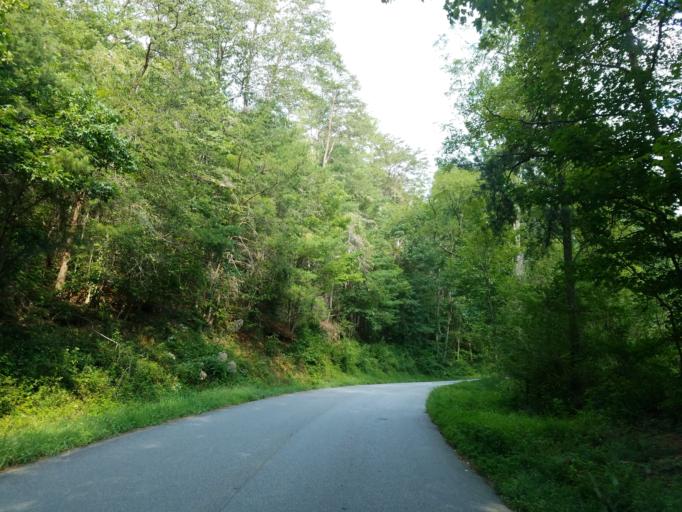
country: US
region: Georgia
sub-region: Fannin County
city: Blue Ridge
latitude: 34.7789
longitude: -84.3889
